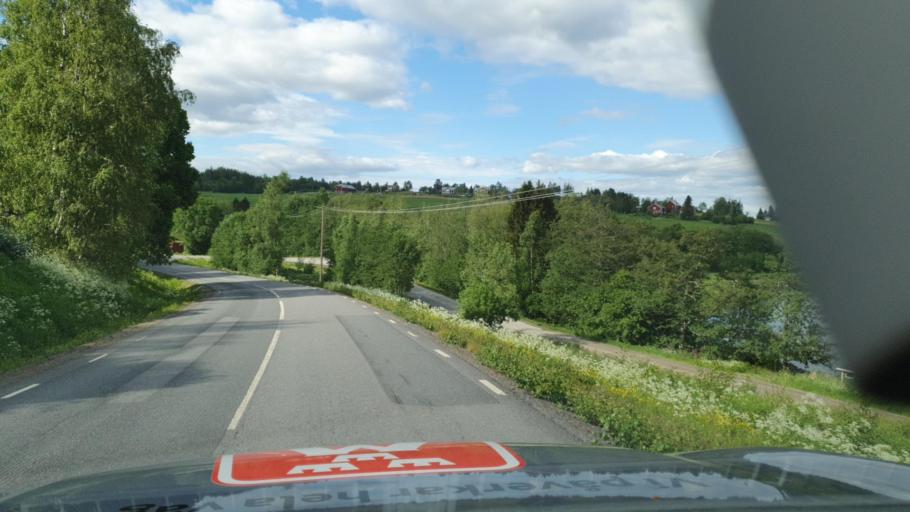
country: SE
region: Vaesternorrland
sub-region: Kramfors Kommun
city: Nordingra
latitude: 62.8392
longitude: 18.2015
